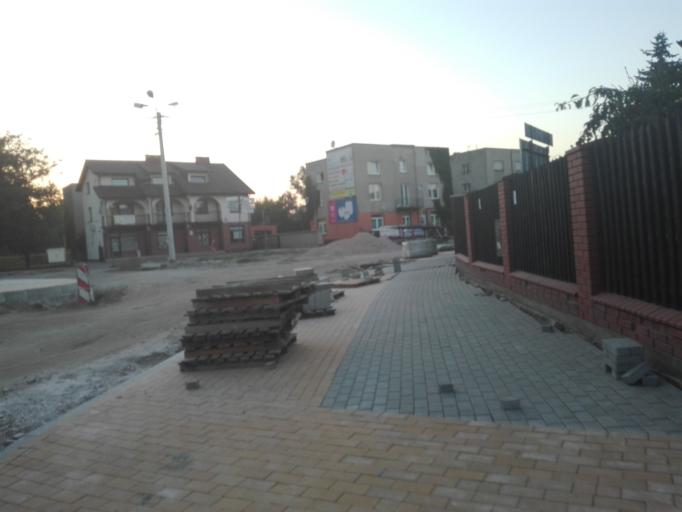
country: PL
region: Masovian Voivodeship
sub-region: Powiat sochaczewski
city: Sochaczew
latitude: 52.2218
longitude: 20.2362
